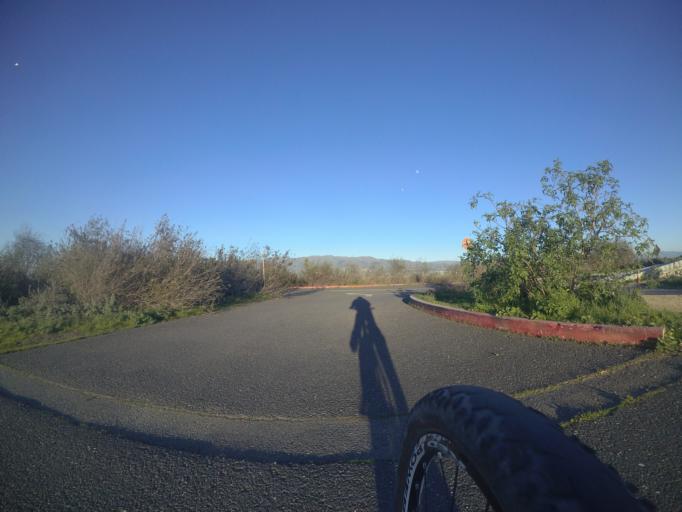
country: US
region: California
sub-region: Santa Clara County
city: Milpitas
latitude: 37.4392
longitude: -121.9590
